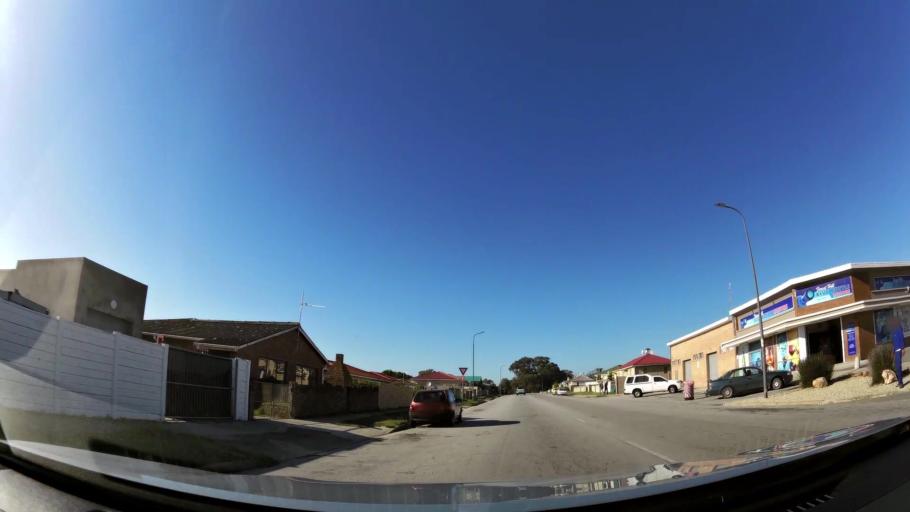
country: ZA
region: Eastern Cape
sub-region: Nelson Mandela Bay Metropolitan Municipality
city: Port Elizabeth
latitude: -33.9828
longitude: 25.6311
